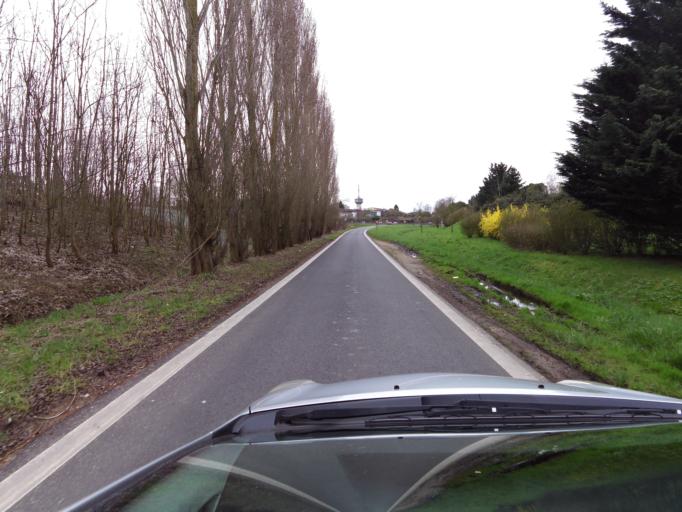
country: FR
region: Ile-de-France
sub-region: Departement de Seine-et-Marne
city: Claye-Souilly
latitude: 48.9478
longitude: 2.6796
